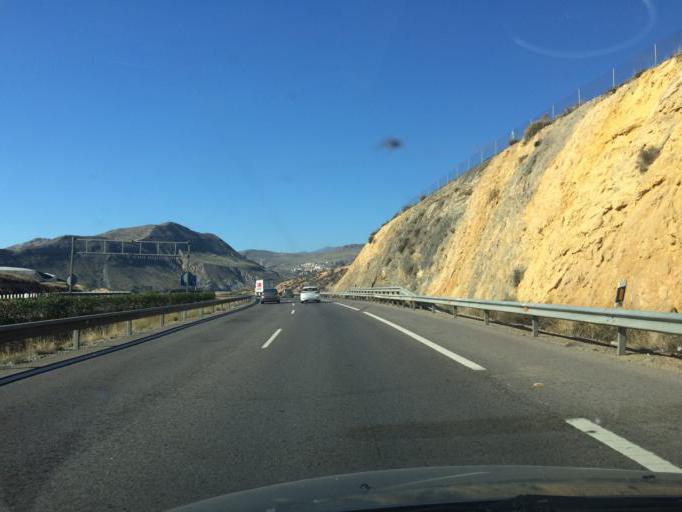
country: ES
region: Andalusia
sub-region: Provincia de Almeria
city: Aguadulce
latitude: 36.8274
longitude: -2.5845
